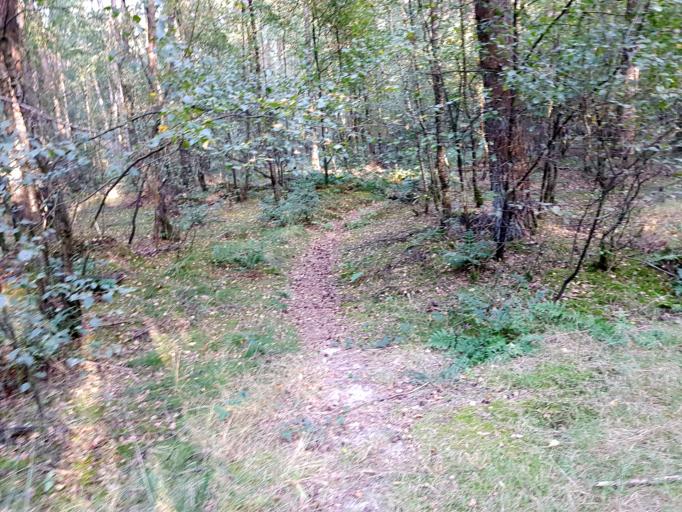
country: NL
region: Utrecht
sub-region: Gemeente Utrechtse Heuvelrug
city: Leersum
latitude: 52.0472
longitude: 5.4431
